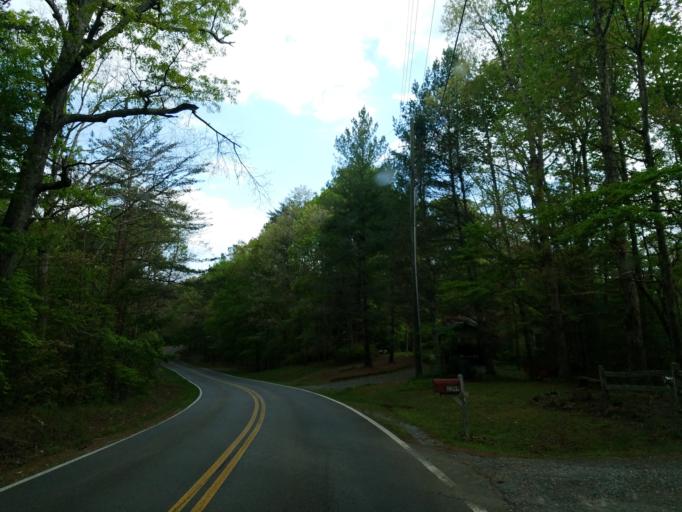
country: US
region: Georgia
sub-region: Pickens County
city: Jasper
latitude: 34.4366
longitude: -84.4631
